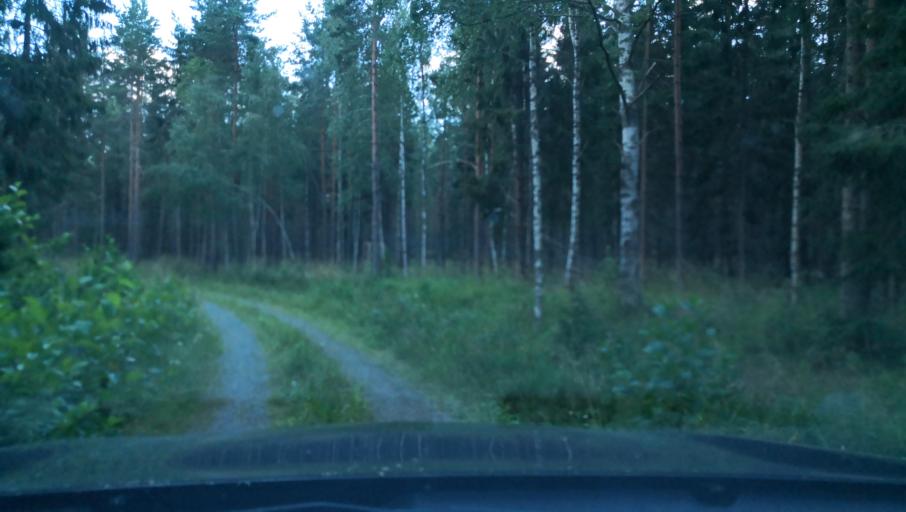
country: SE
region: Vaestmanland
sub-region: Vasteras
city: Skultuna
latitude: 59.7312
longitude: 16.3852
